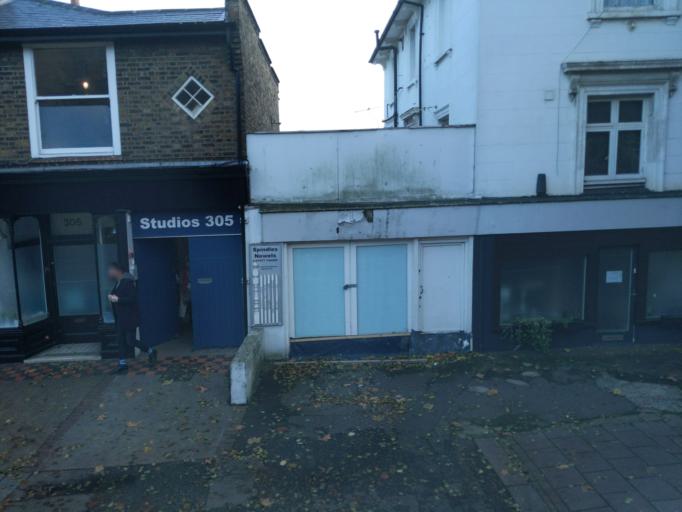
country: GB
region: England
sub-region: Greater London
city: Hammersmith
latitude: 51.4989
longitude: -0.2424
